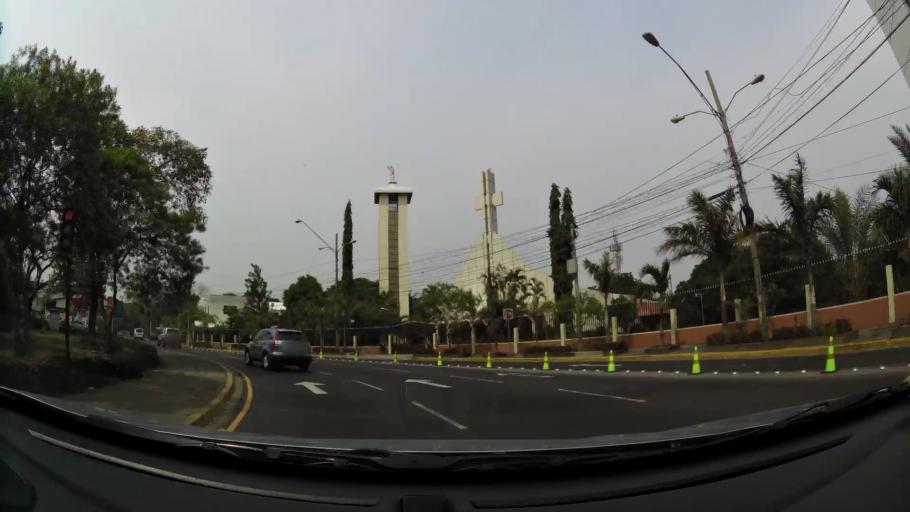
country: HN
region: Cortes
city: San Pedro Sula
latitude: 15.4966
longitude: -88.0336
